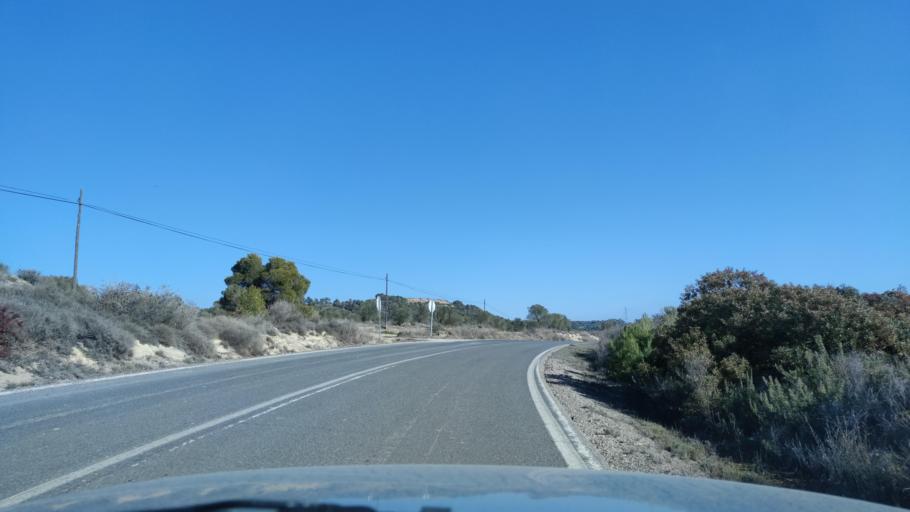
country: ES
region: Catalonia
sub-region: Provincia de Lleida
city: Maials
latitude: 41.3330
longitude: 0.4431
